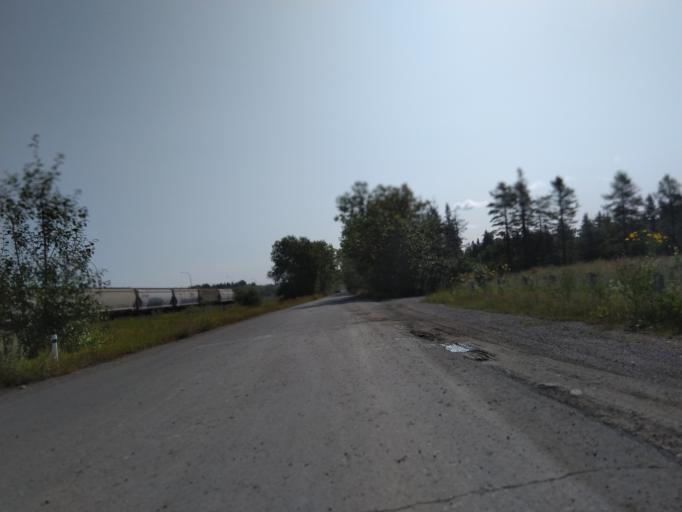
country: CA
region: Alberta
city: Calgary
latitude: 51.1021
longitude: -114.2266
